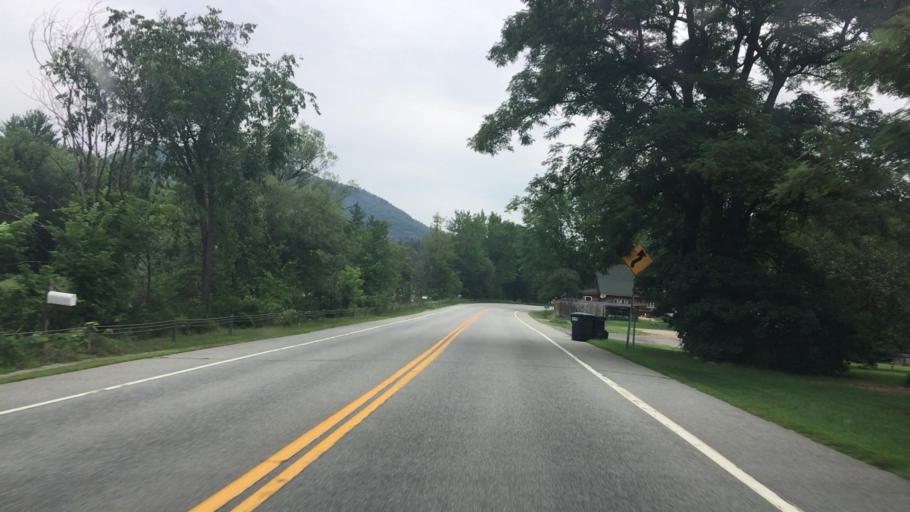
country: US
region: New York
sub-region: Essex County
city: Lake Placid
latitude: 44.3257
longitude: -73.7750
